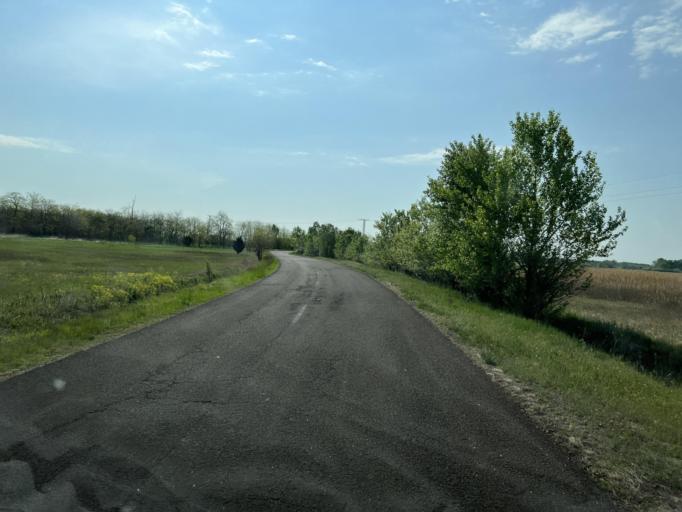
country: HU
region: Pest
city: Jaszkarajeno
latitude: 47.0119
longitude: 20.0473
